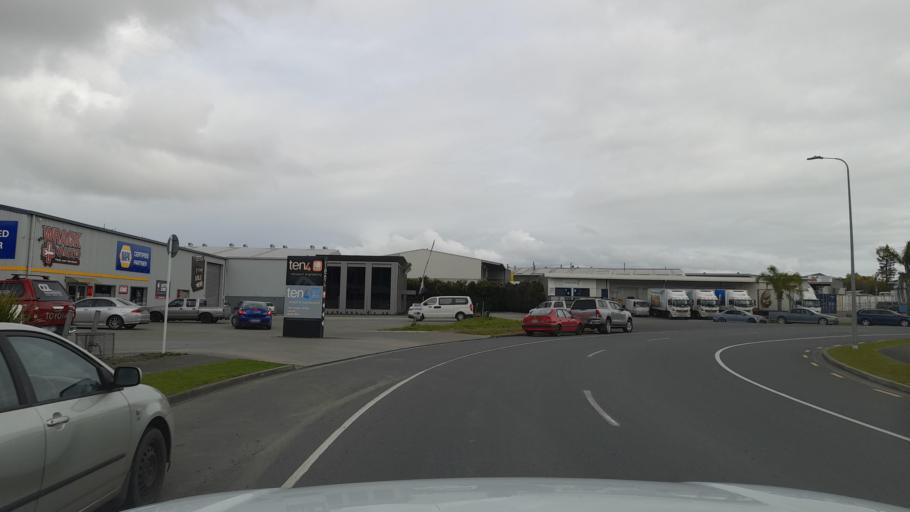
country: NZ
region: Northland
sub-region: Whangarei
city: Whangarei
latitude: -35.7494
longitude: 174.3131
